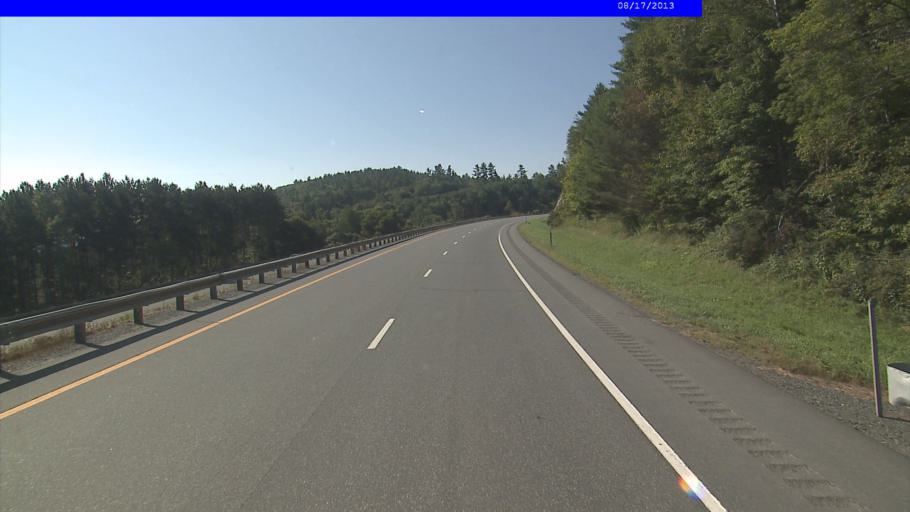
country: US
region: Vermont
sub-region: Windsor County
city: Windsor
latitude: 43.5106
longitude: -72.4065
